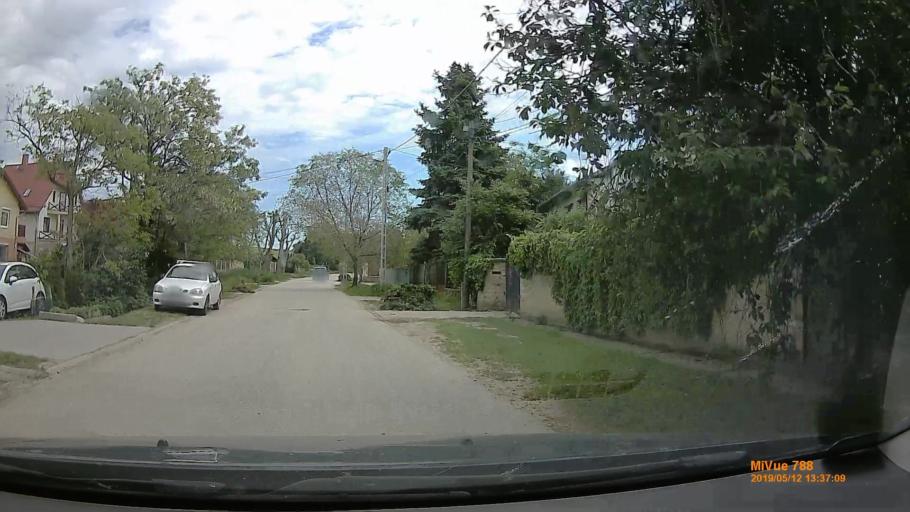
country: HU
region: Pest
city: Pecel
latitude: 47.4799
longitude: 19.2990
